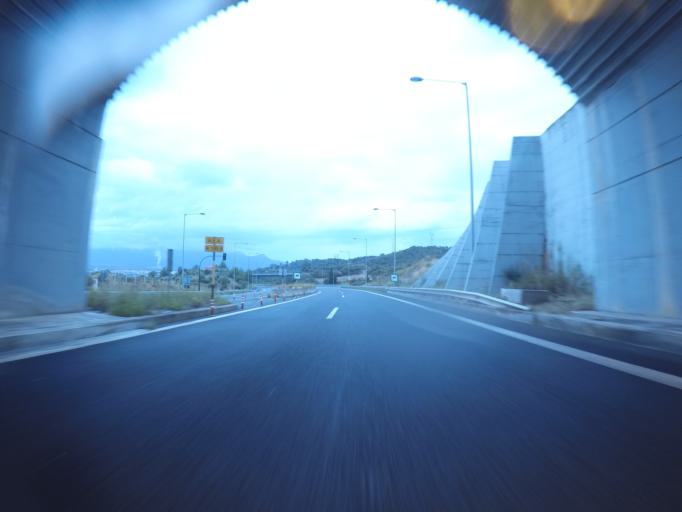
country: GR
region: Peloponnese
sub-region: Nomos Arkadias
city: Megalopoli
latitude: 37.3929
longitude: 22.1843
